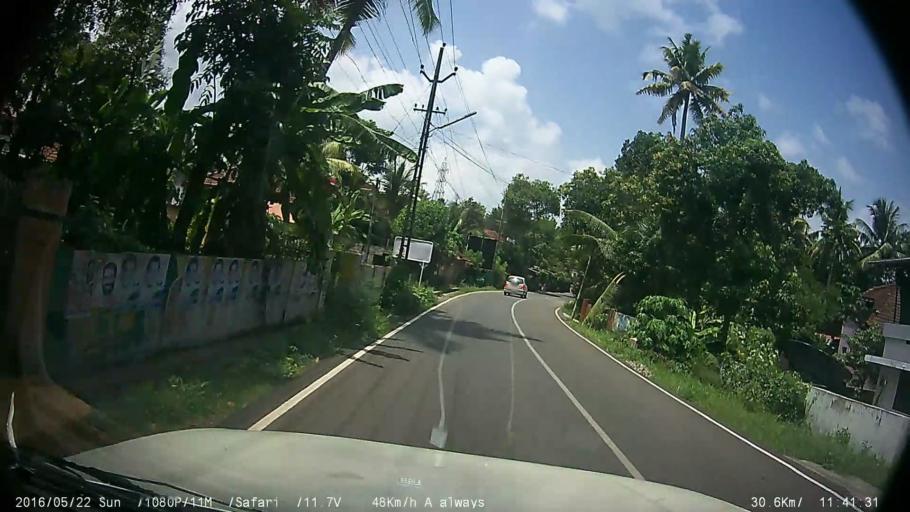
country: IN
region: Kerala
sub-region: Kottayam
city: Kottayam
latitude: 9.5478
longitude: 76.5189
